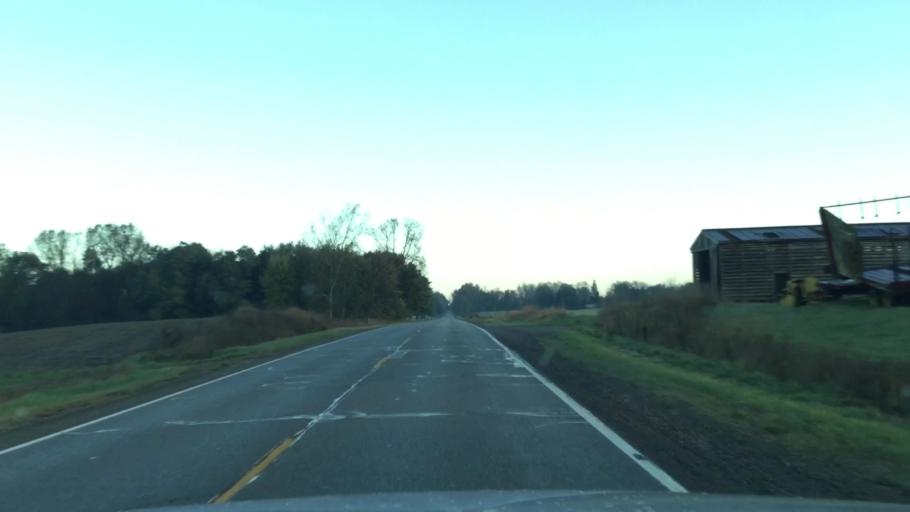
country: US
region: Michigan
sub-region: Livingston County
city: Howell
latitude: 42.6744
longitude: -83.9362
